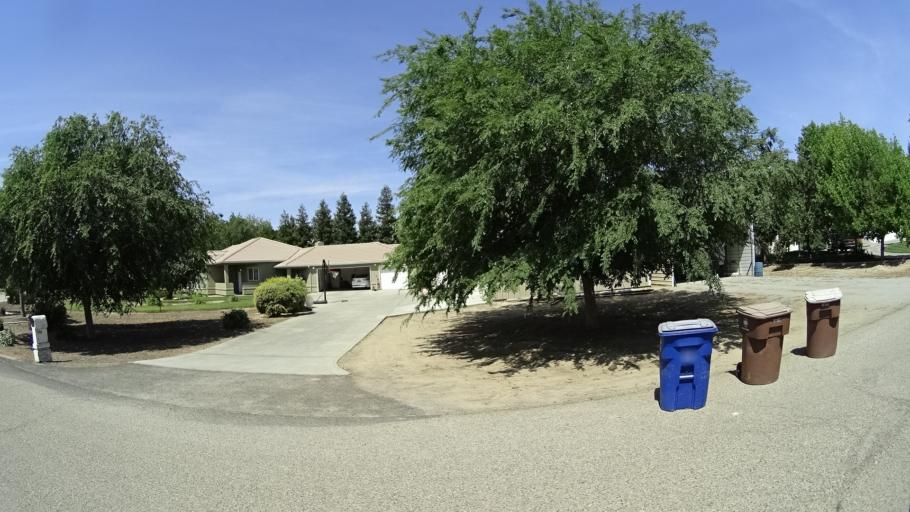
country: US
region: California
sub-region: Kings County
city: Armona
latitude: 36.3403
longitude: -119.7023
